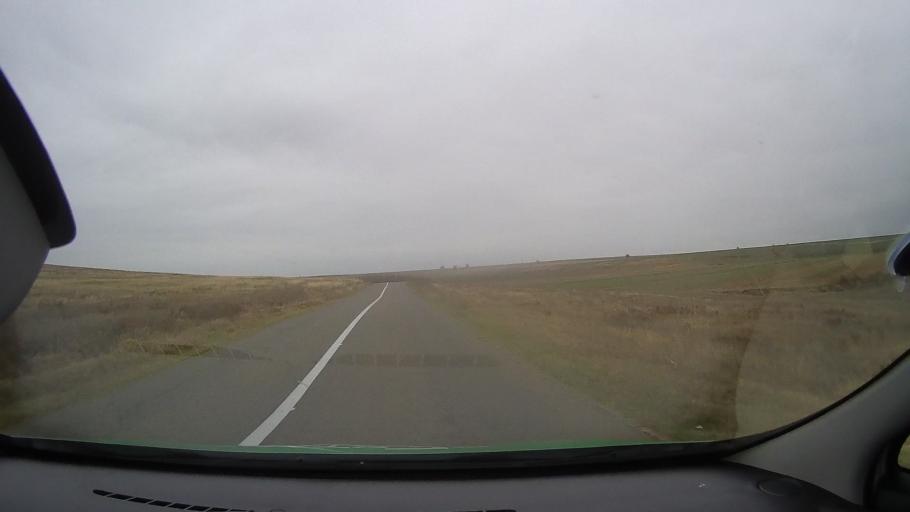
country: RO
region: Constanta
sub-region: Comuna Saraiu
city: Saraiu
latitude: 44.7255
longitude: 28.1820
